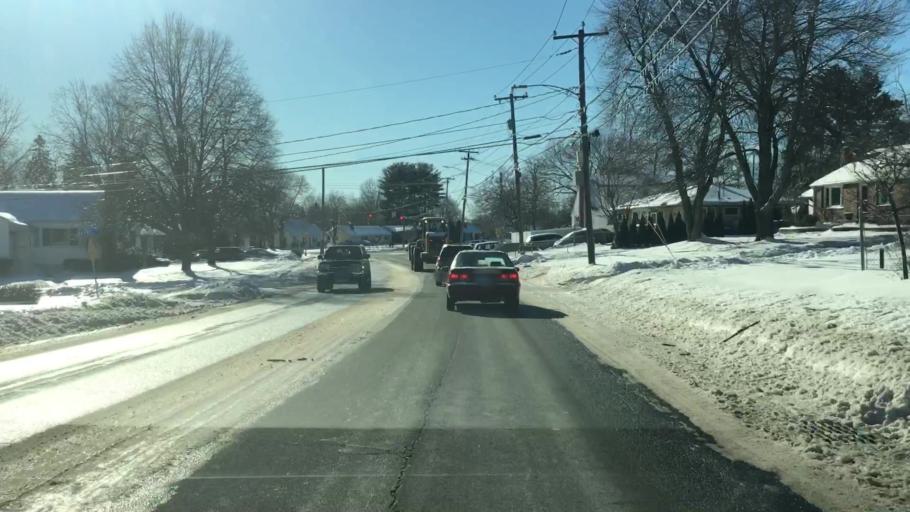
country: US
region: Connecticut
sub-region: Hartford County
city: Newington
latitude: 41.7173
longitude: -72.7429
